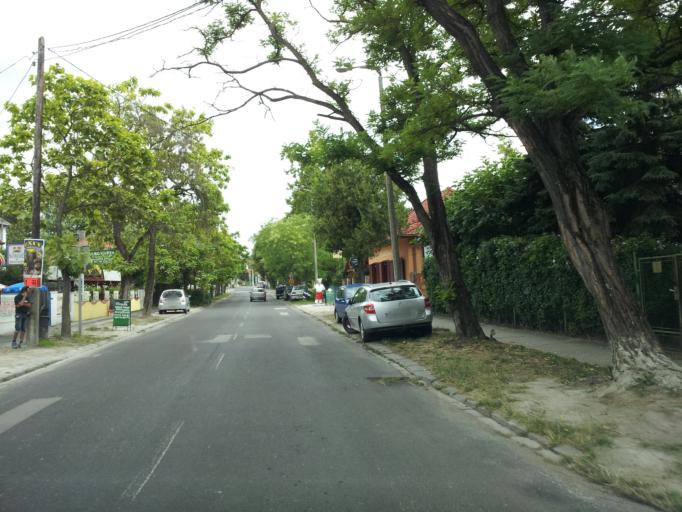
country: HU
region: Somogy
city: Siofok
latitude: 46.8992
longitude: 18.0171
